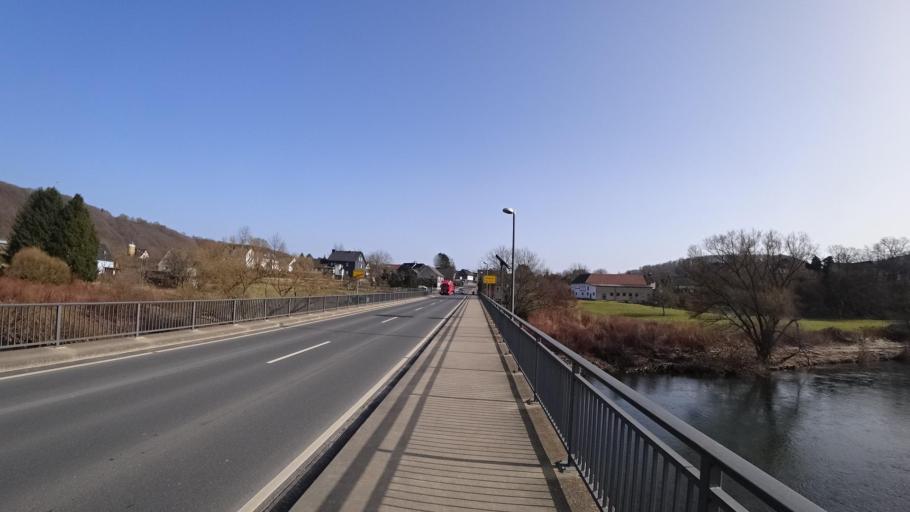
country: DE
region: Rheinland-Pfalz
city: Etzbach
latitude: 50.7794
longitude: 7.6823
